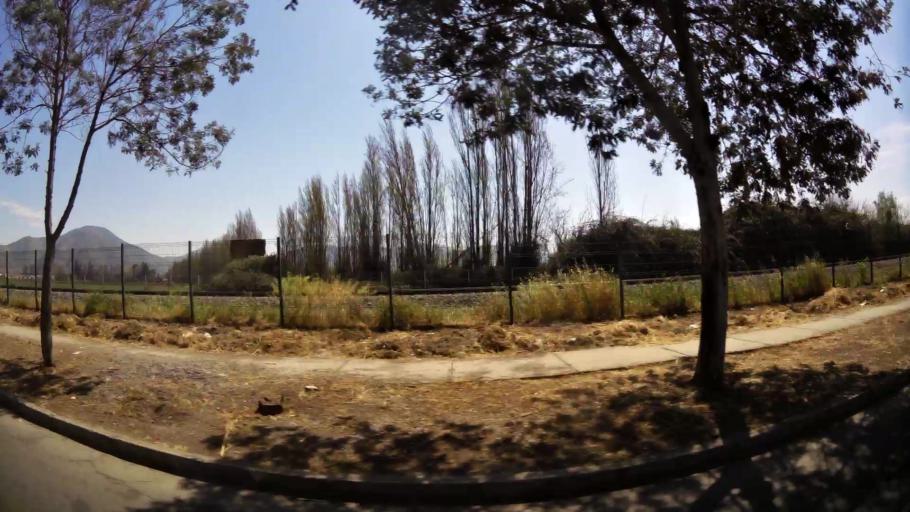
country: CL
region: Santiago Metropolitan
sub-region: Provincia de Talagante
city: Talagante
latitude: -33.6541
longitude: -70.9134
